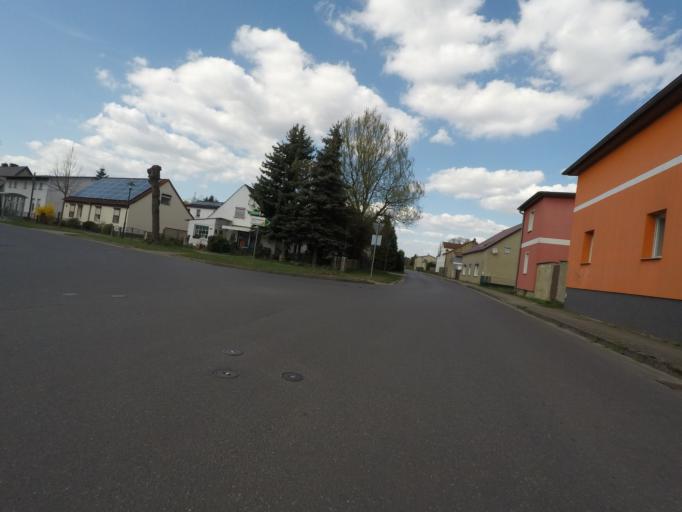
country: DE
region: Brandenburg
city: Melchow
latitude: 52.8530
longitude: 13.6818
